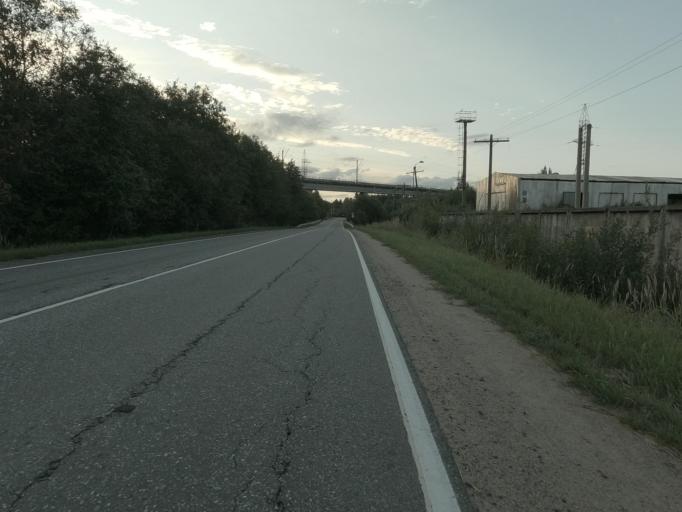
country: RU
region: Leningrad
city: Mga
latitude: 59.7575
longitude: 31.0198
